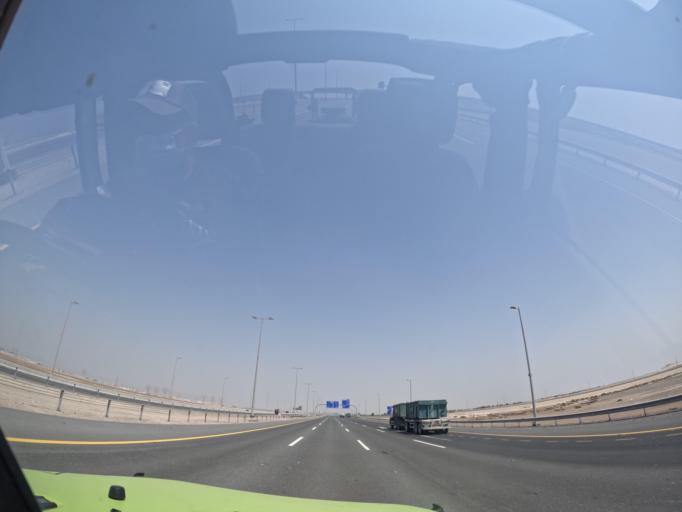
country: AE
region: Abu Dhabi
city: Abu Dhabi
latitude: 24.2791
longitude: 54.5278
